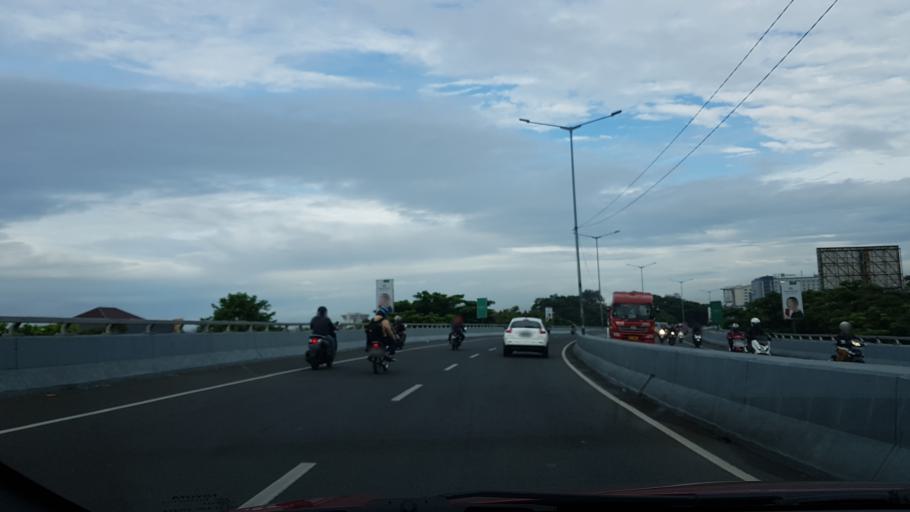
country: ID
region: West Java
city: Bandung
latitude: -6.9002
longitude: 107.5961
